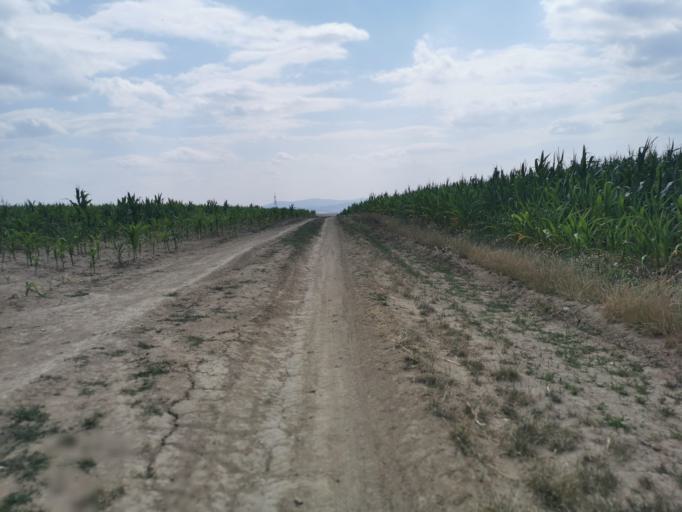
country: SK
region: Trnavsky
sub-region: Okres Senica
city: Senica
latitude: 48.6910
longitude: 17.4208
